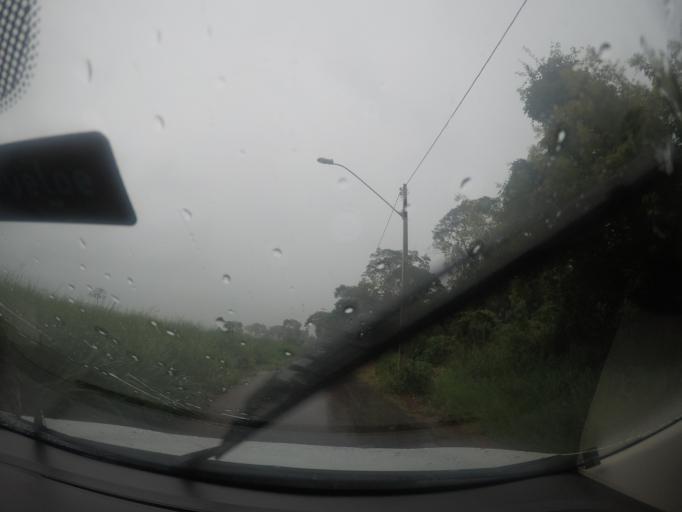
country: BR
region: Goias
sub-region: Goiania
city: Goiania
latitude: -16.5937
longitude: -49.3243
